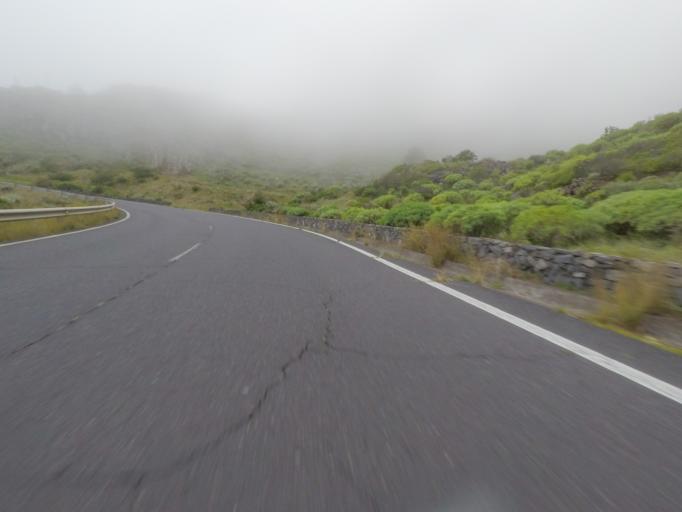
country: ES
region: Canary Islands
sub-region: Provincia de Santa Cruz de Tenerife
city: Alajero
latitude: 28.0961
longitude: -17.2006
